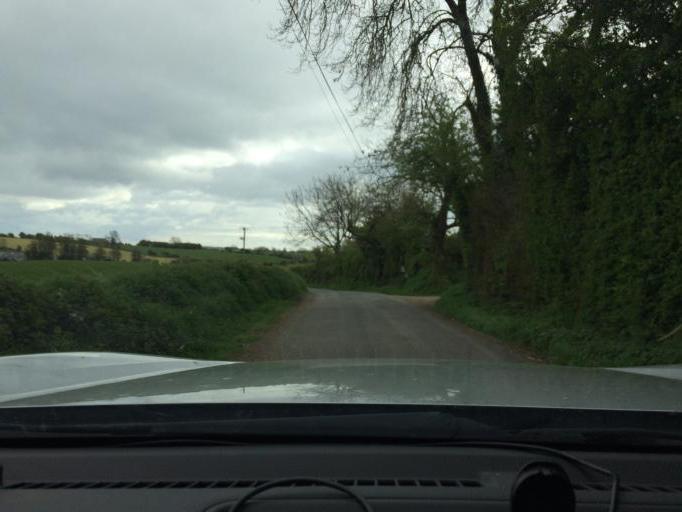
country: IE
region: Munster
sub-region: Waterford
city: Dungarvan
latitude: 52.0546
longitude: -7.6180
